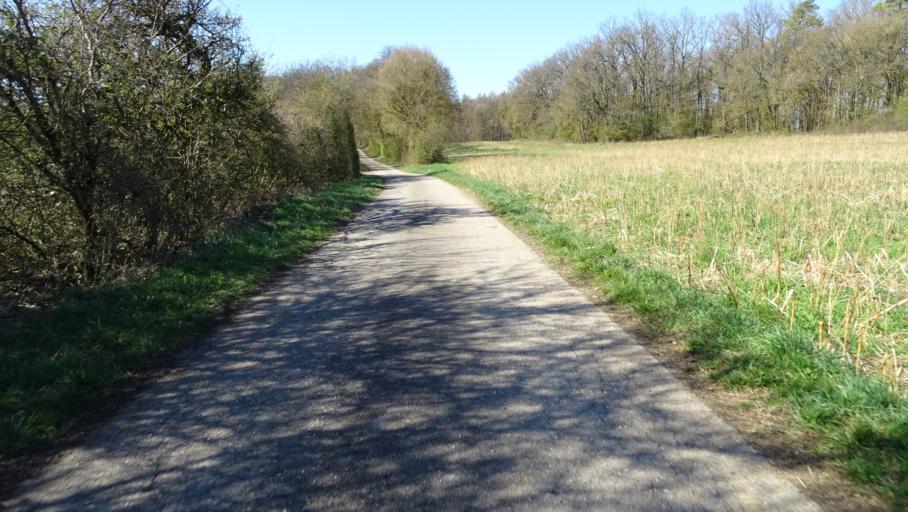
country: DE
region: Baden-Wuerttemberg
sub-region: Karlsruhe Region
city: Seckach
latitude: 49.4305
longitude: 9.3532
